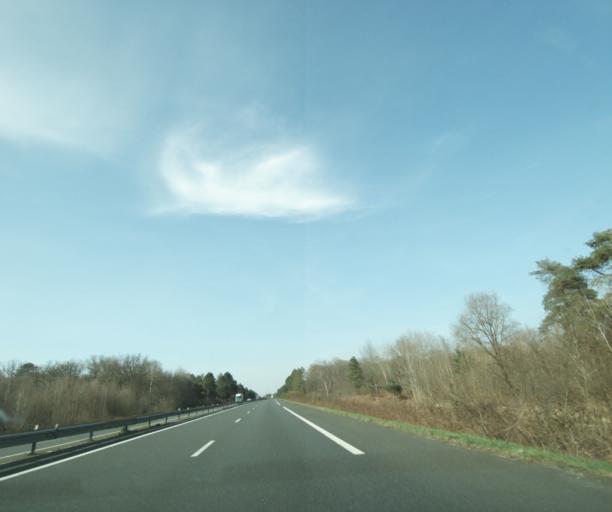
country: FR
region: Centre
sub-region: Departement du Loir-et-Cher
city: Chaumont-sur-Tharonne
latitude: 47.6164
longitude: 1.9637
